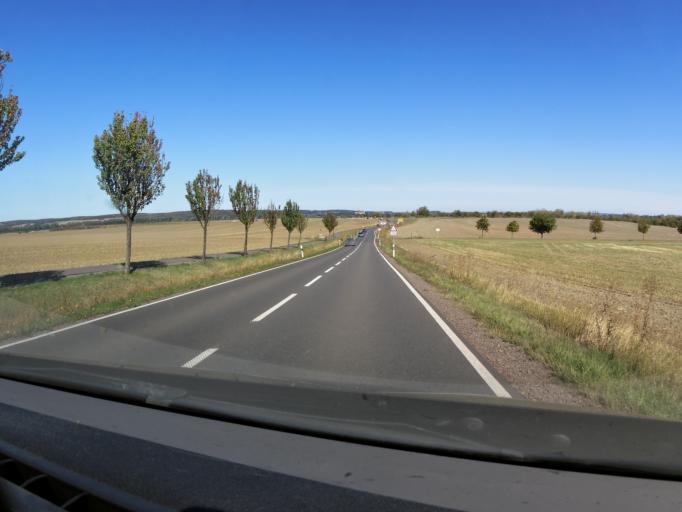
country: DE
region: Saxony-Anhalt
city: Bad Suderode
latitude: 51.7431
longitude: 11.1206
